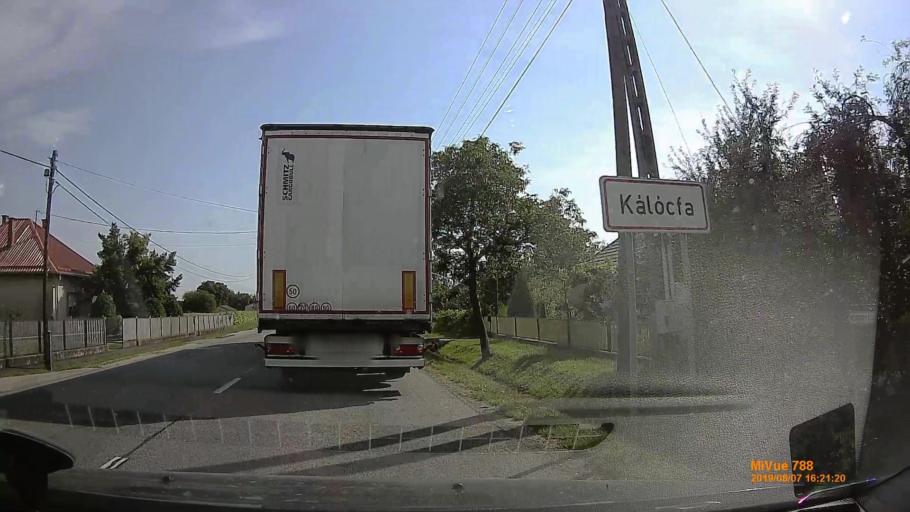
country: HU
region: Zala
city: Zalalovo
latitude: 46.7638
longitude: 16.5648
